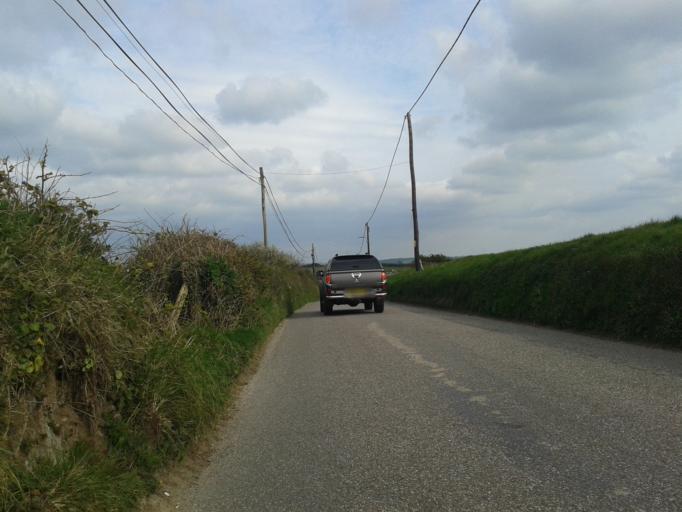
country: GB
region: England
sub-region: Devon
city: Braunton
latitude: 51.1762
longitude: -4.1744
